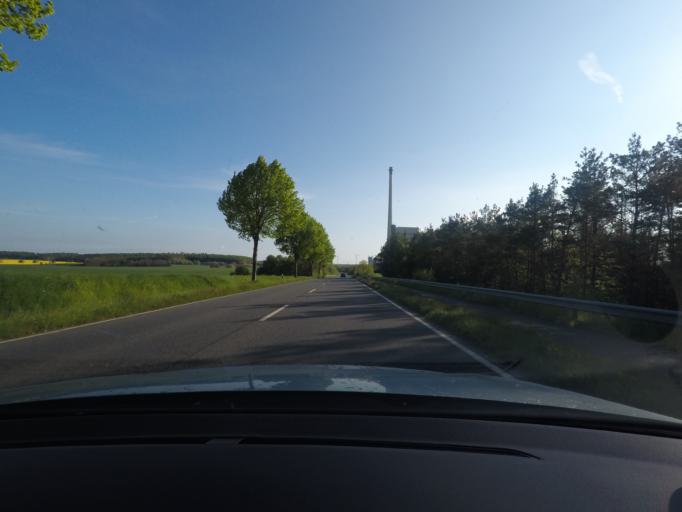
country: DE
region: Lower Saxony
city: Schoningen
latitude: 52.1648
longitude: 10.9684
